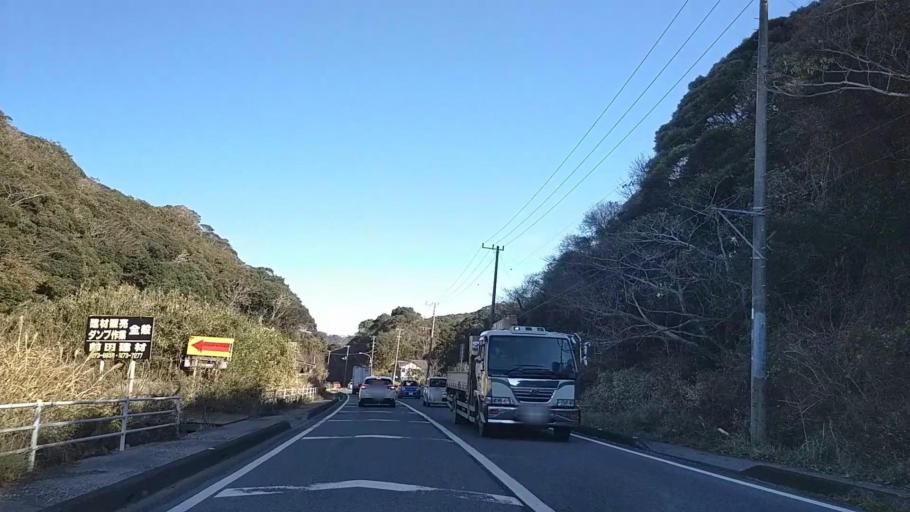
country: JP
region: Chiba
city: Katsuura
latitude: 35.1262
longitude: 140.2353
